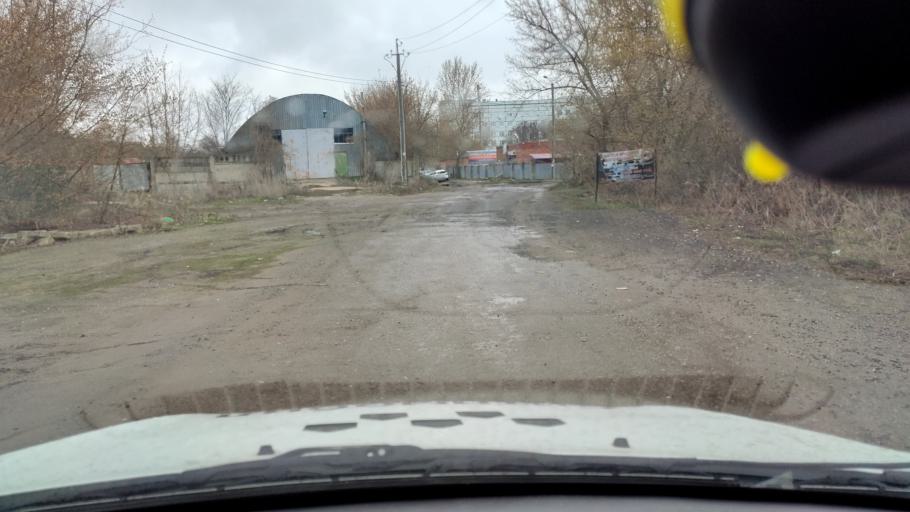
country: RU
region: Samara
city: Tol'yatti
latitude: 53.5263
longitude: 49.3918
